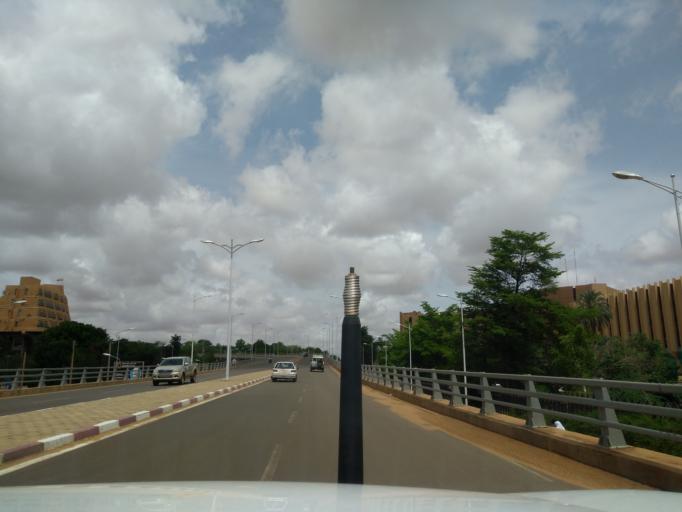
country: NE
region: Niamey
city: Niamey
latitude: 13.5083
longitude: 2.1094
